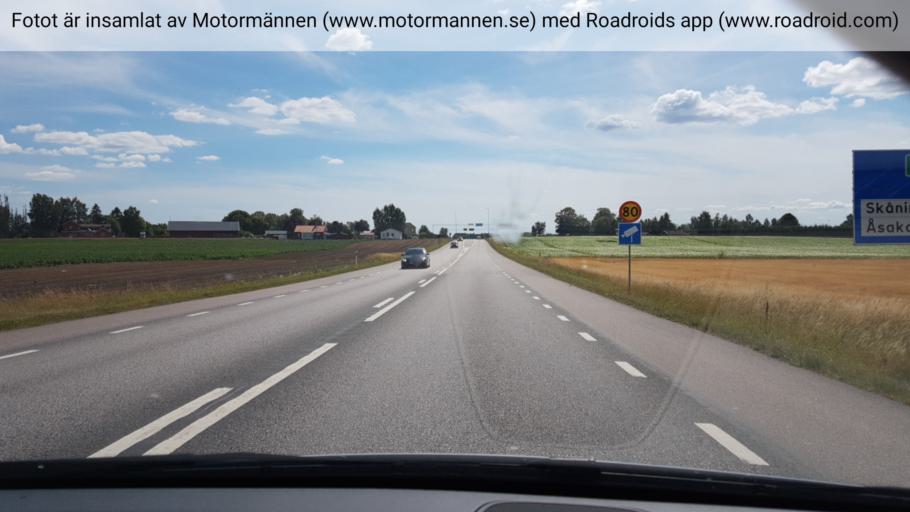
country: SE
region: Vaestra Goetaland
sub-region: Skara Kommun
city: Skara
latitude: 58.4353
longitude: 13.4710
